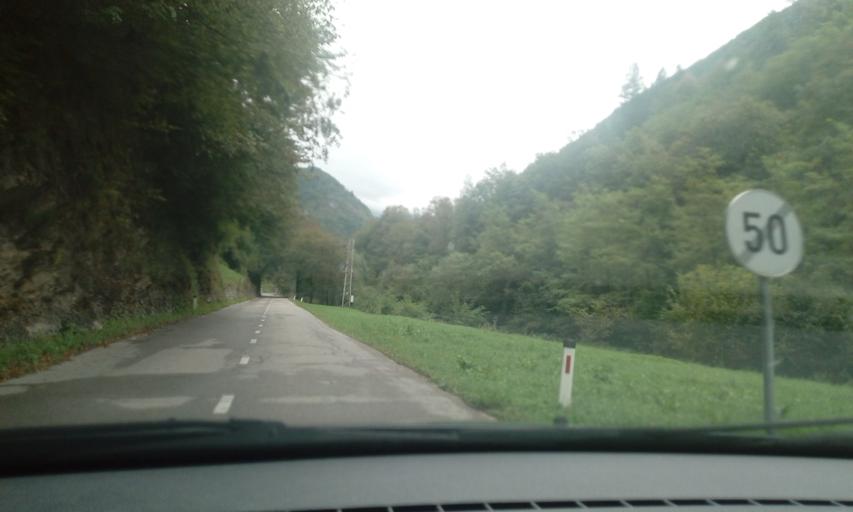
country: SI
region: Bohinj
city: Bohinjska Bistrica
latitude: 46.1936
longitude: 13.9316
